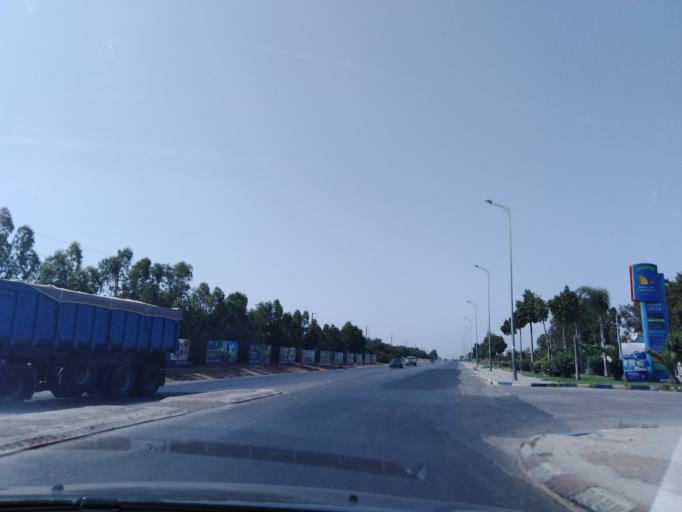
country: MA
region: Chaouia-Ouardigha
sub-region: Settat Province
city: Berrechid
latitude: 33.2522
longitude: -7.5843
